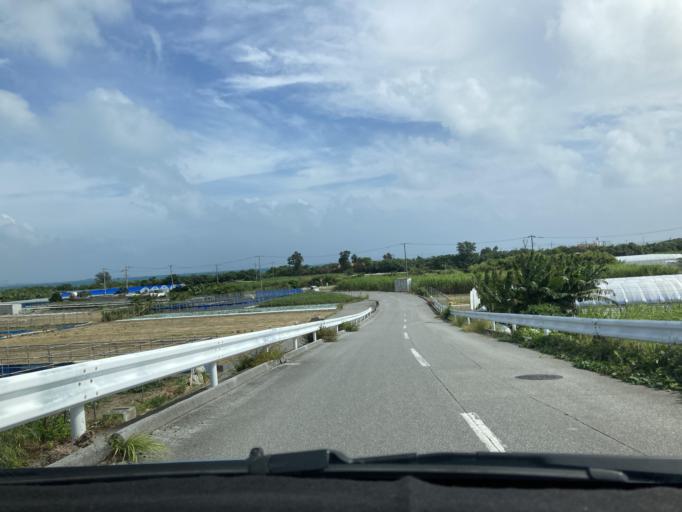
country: JP
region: Okinawa
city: Ginowan
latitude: 26.1525
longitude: 127.8051
